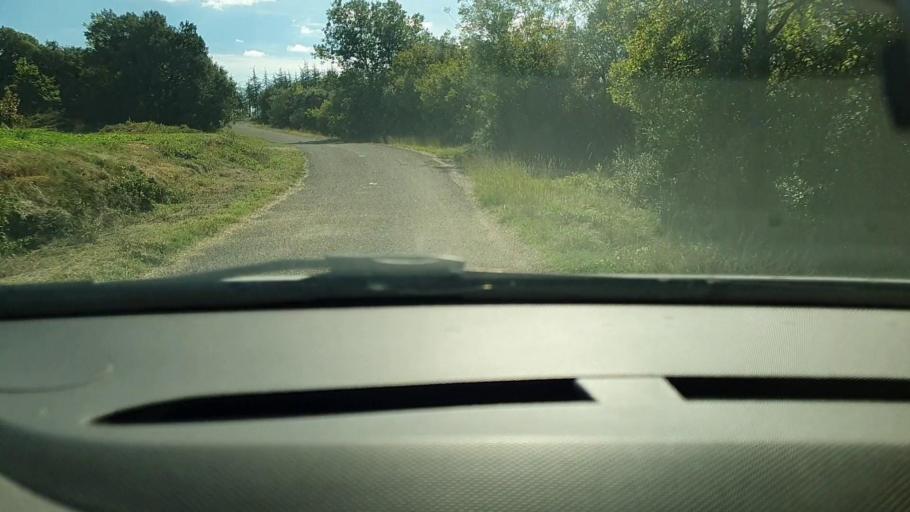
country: FR
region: Languedoc-Roussillon
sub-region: Departement du Gard
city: Barjac
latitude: 44.1942
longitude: 4.3159
